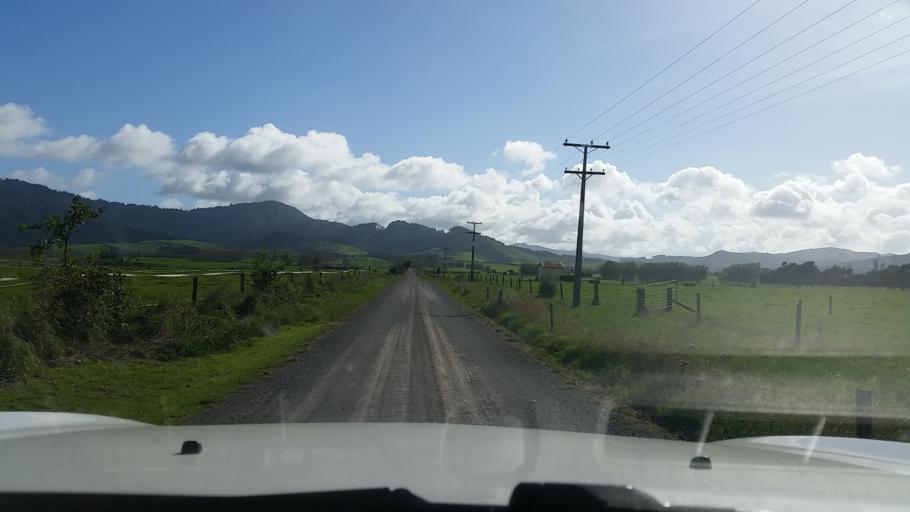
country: NZ
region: Waikato
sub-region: Hauraki District
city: Ngatea
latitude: -37.5153
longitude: 175.4104
